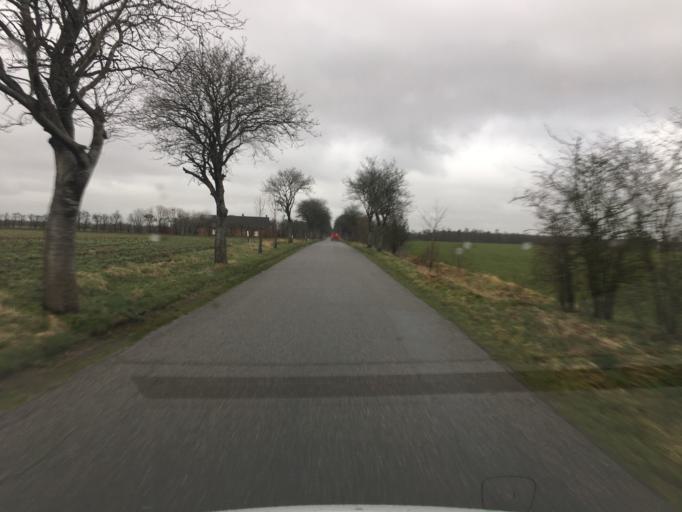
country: DK
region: South Denmark
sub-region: Aabenraa Kommune
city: Tinglev
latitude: 54.9023
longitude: 9.3018
